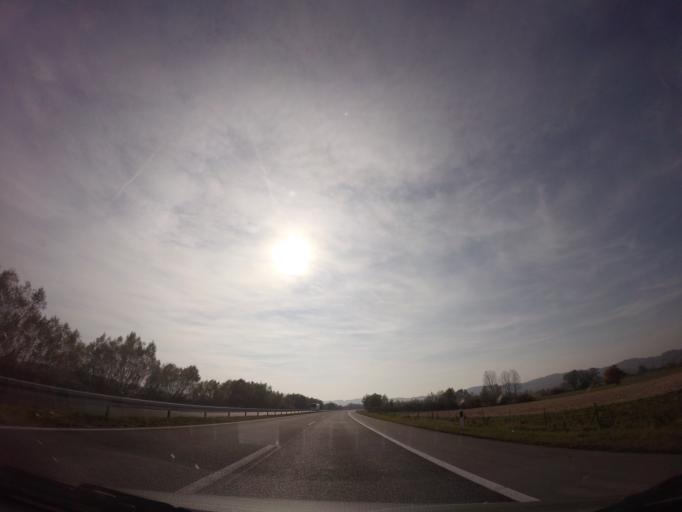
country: HR
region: Zagrebacka
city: Brckovljani
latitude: 45.9554
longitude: 16.2797
